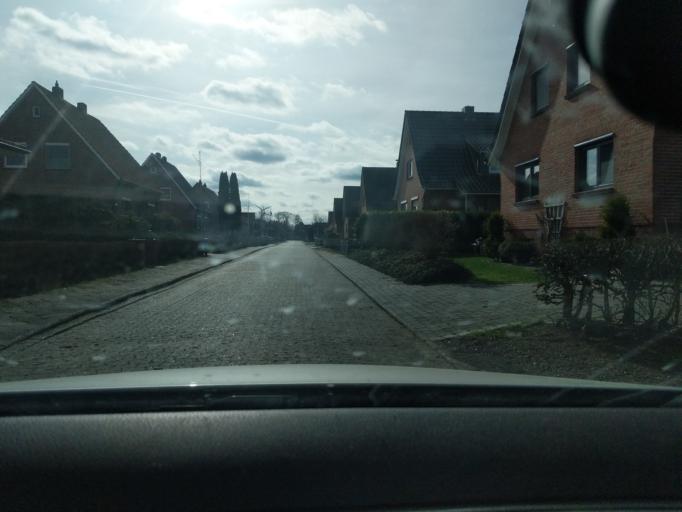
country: DE
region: Lower Saxony
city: Drochtersen
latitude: 53.7116
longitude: 9.3896
